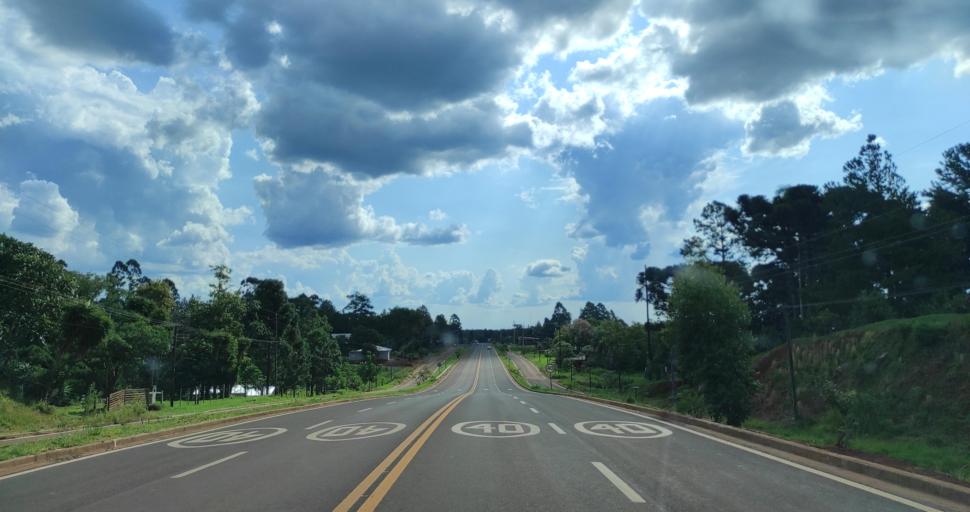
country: AR
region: Misiones
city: Bernardo de Irigoyen
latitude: -26.2928
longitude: -53.7411
